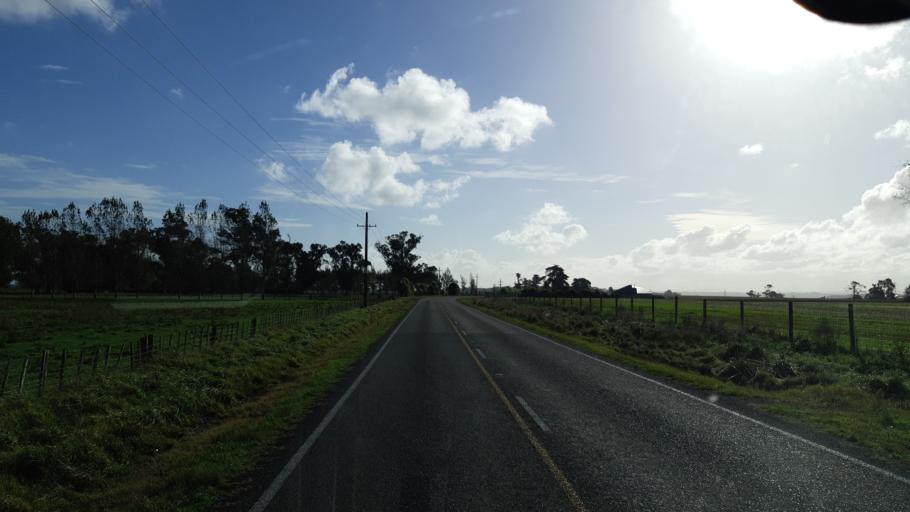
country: NZ
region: Manawatu-Wanganui
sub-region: Wanganui District
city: Wanganui
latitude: -39.9587
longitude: 175.1811
